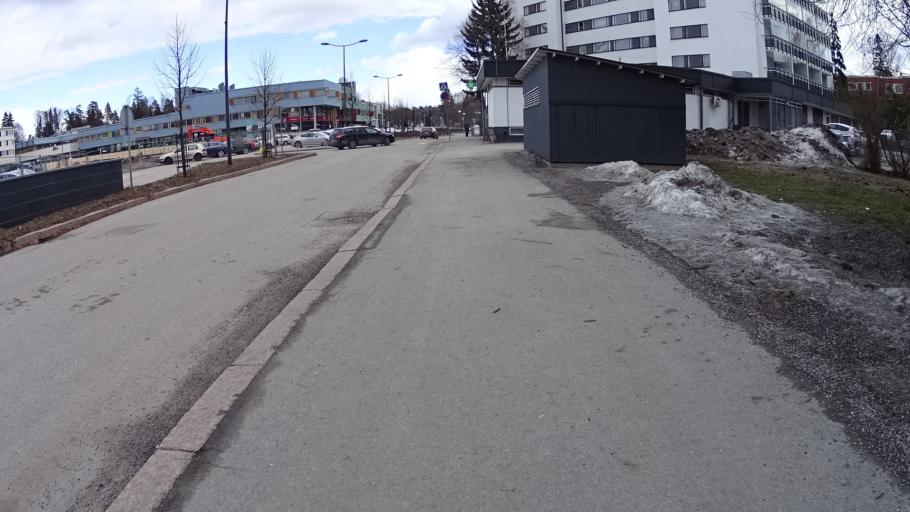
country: FI
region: Uusimaa
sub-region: Helsinki
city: Kauniainen
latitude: 60.2101
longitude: 24.7260
